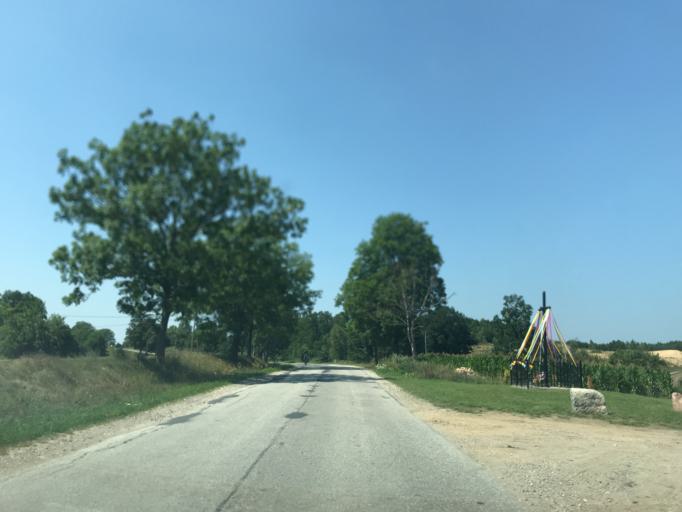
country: PL
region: Kujawsko-Pomorskie
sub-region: Powiat lipnowski
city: Chrostkowo
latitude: 52.9898
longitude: 19.2897
